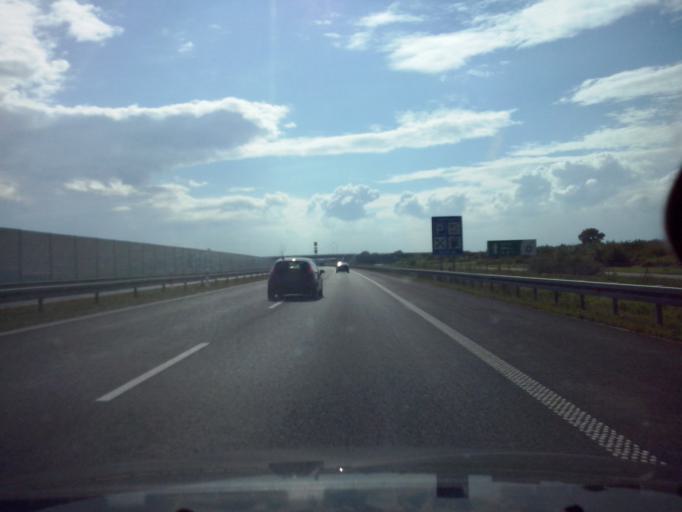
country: PL
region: Lesser Poland Voivodeship
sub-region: Powiat tarnowski
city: Wierzchoslawice
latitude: 50.0480
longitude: 20.8999
